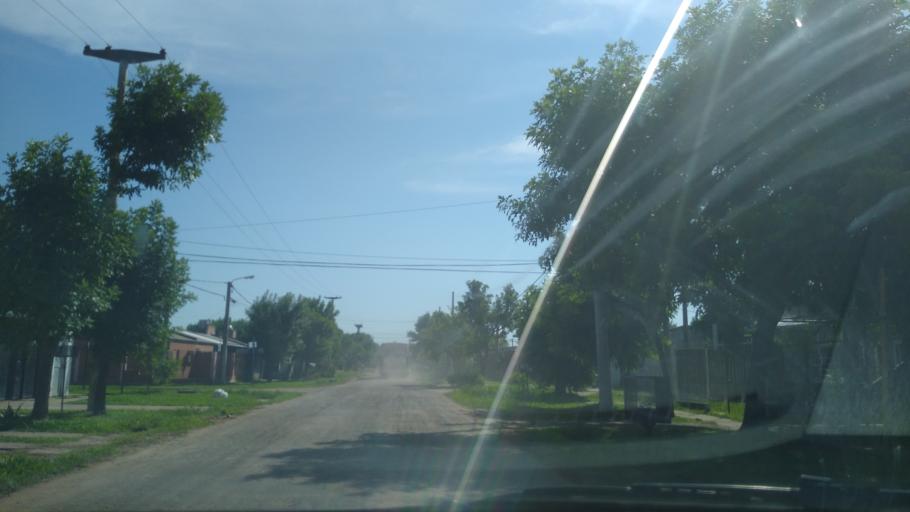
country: AR
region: Chaco
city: Barranqueras
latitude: -27.4922
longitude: -58.9569
